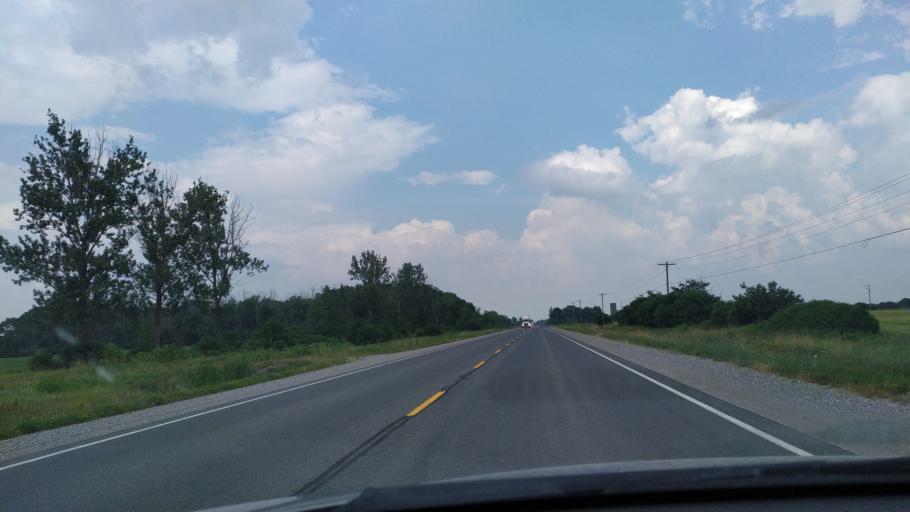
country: CA
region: Ontario
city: Stratford
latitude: 43.2354
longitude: -81.1195
